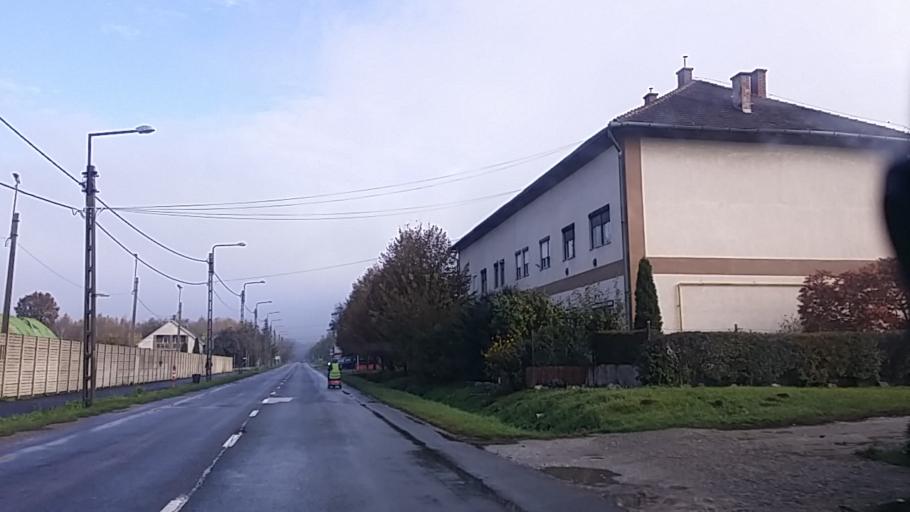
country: HU
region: Heves
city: Belapatfalva
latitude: 48.0604
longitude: 20.3537
